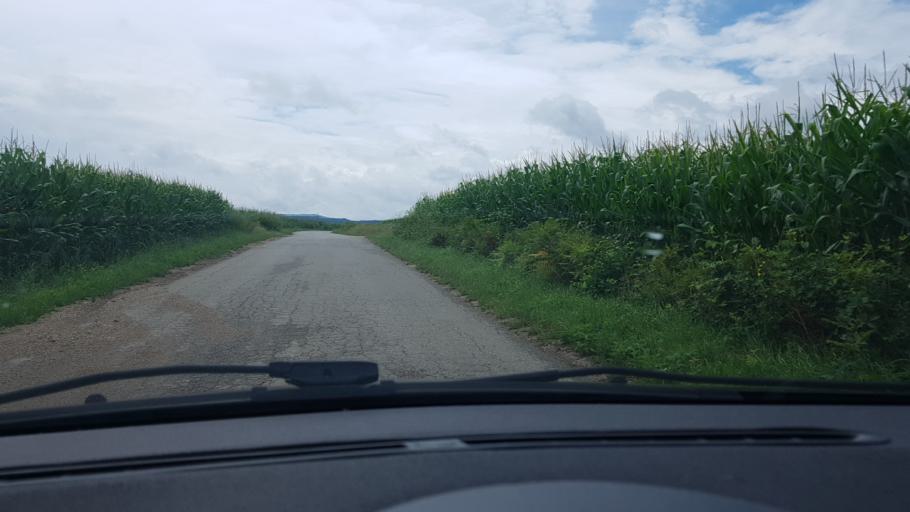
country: HR
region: Licko-Senjska
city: Jezerce
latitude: 44.9583
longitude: 15.6823
